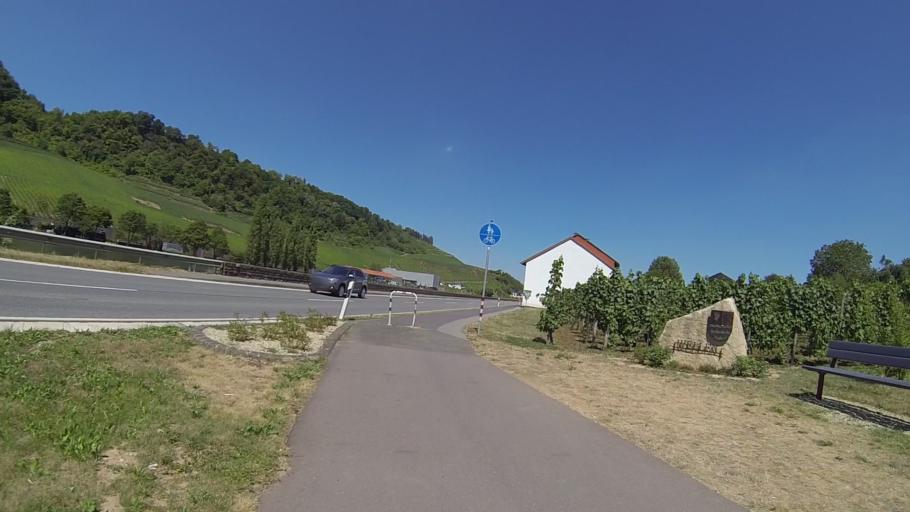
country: DE
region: Rheinland-Pfalz
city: Wellen
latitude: 49.6675
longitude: 6.4302
